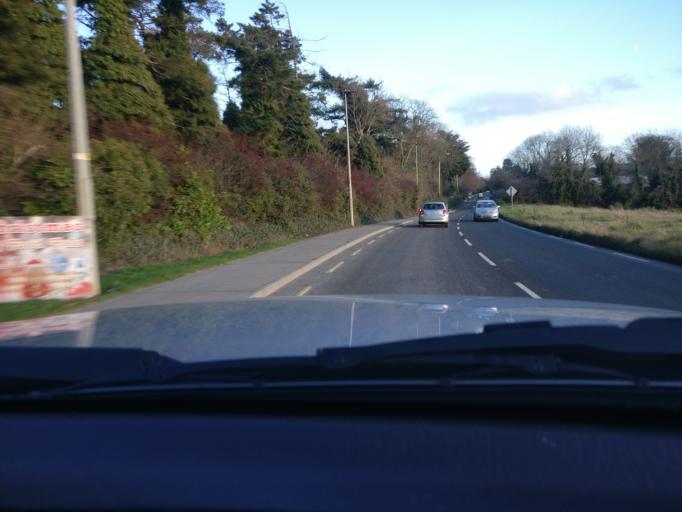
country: IE
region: Leinster
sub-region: Lu
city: Ardee
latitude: 53.8565
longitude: -6.5525
